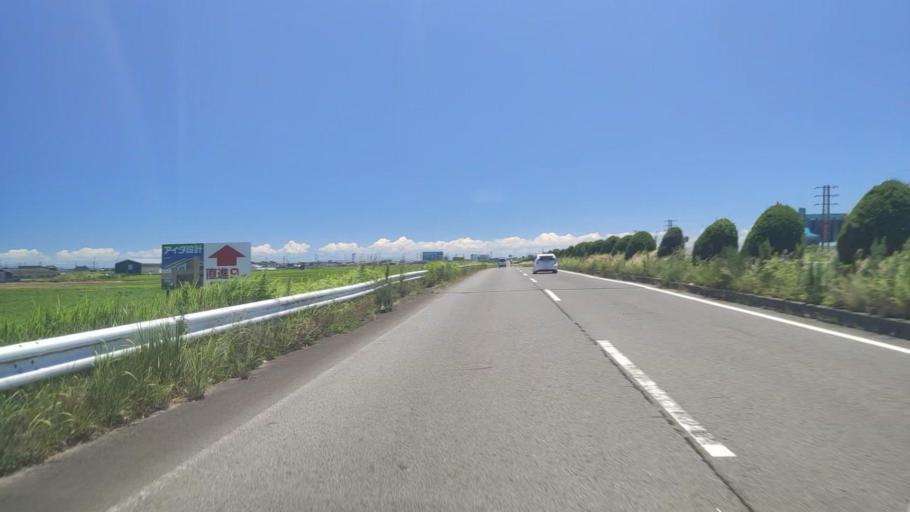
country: JP
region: Mie
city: Suzuka
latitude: 34.8893
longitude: 136.5999
